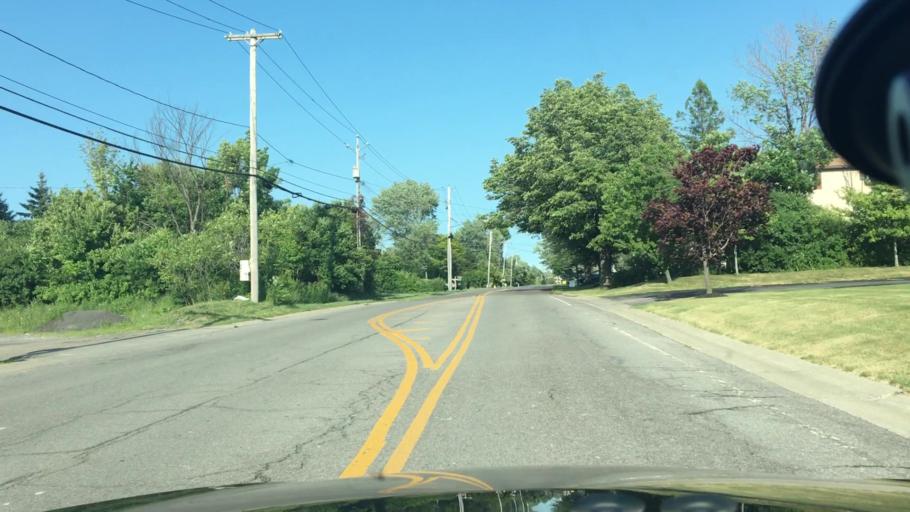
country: US
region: New York
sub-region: Erie County
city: Wanakah
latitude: 42.7583
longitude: -78.8605
